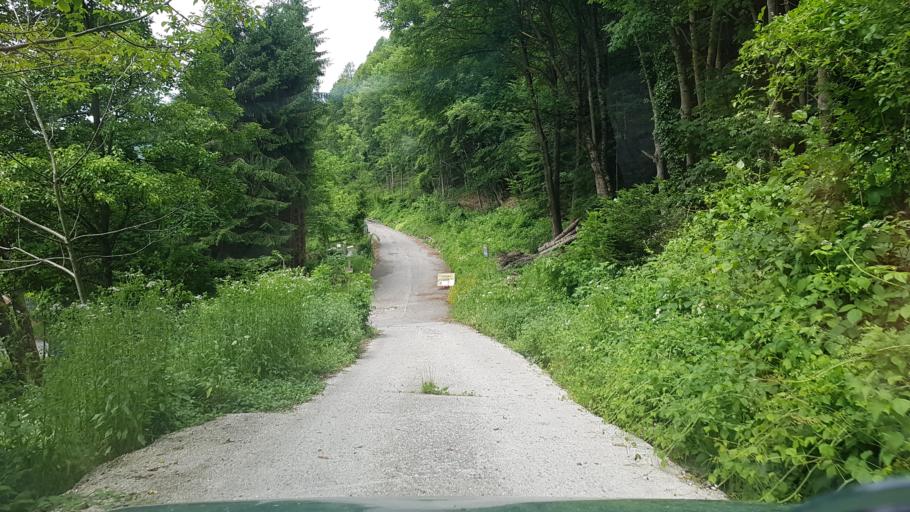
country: IT
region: Friuli Venezia Giulia
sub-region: Provincia di Udine
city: Torreano
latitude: 46.1777
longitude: 13.4300
